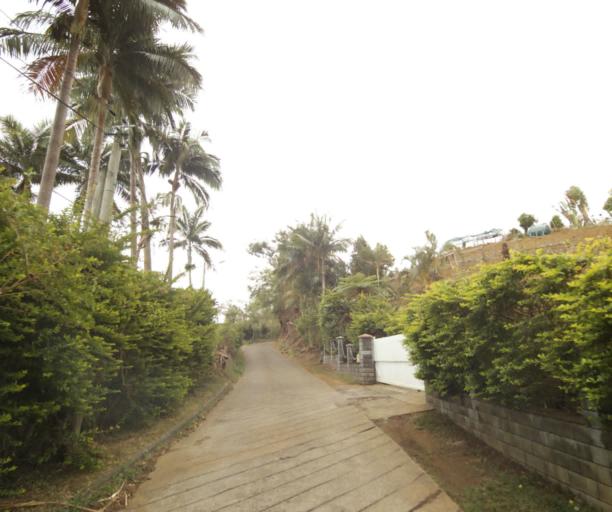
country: RE
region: Reunion
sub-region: Reunion
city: Saint-Paul
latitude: -21.0161
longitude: 55.3342
